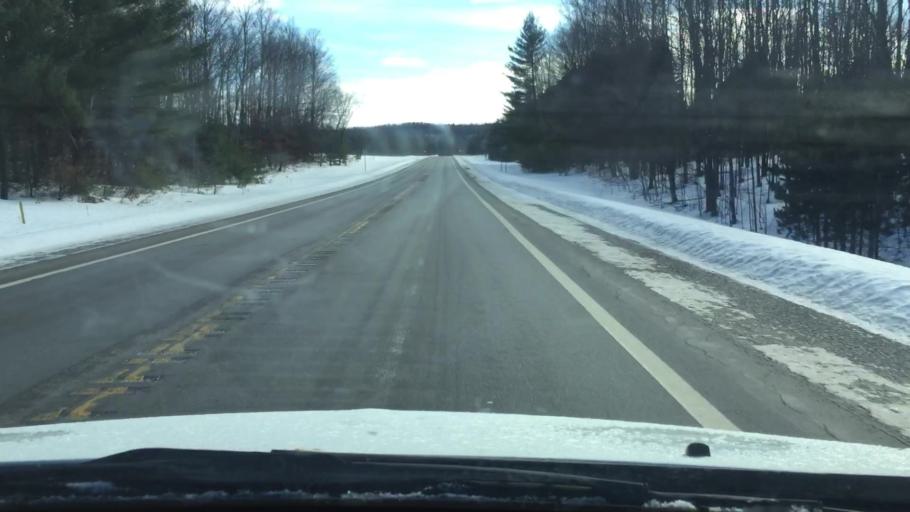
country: US
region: Michigan
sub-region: Antrim County
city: Mancelona
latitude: 44.9656
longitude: -85.0530
